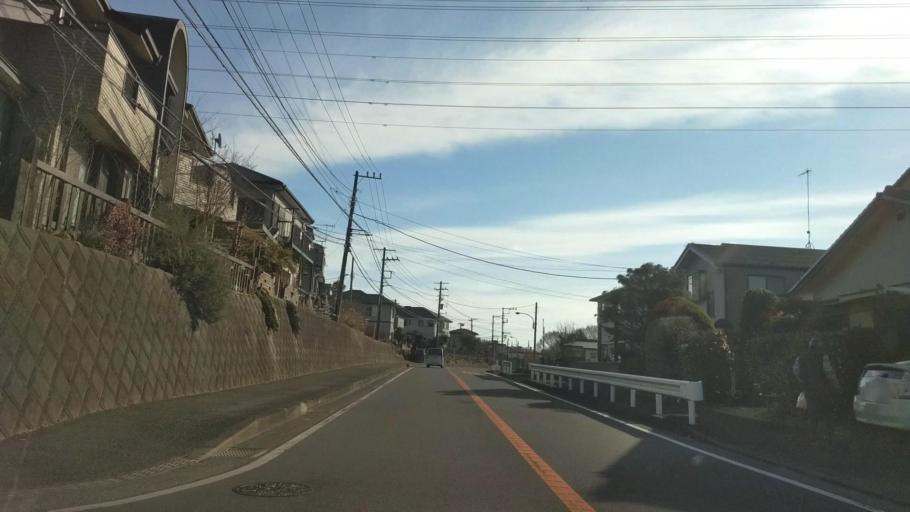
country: JP
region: Kanagawa
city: Hadano
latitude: 35.3890
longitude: 139.2355
